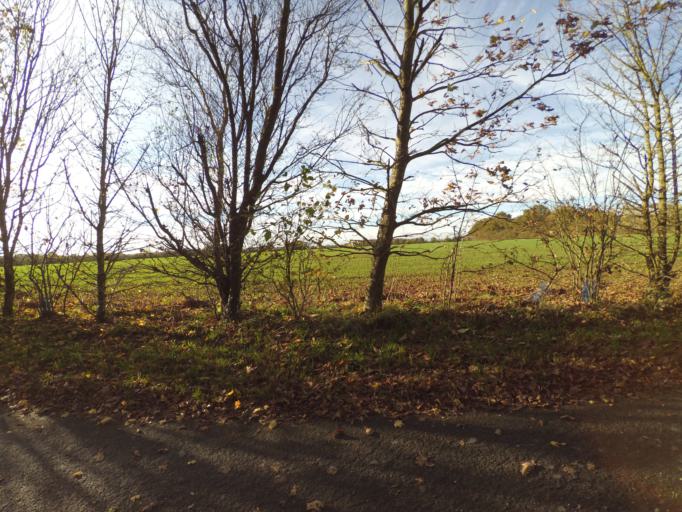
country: FR
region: Pays de la Loire
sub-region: Departement de la Vendee
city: Saint-Hilaire-de-Loulay
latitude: 47.0069
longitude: -1.3415
